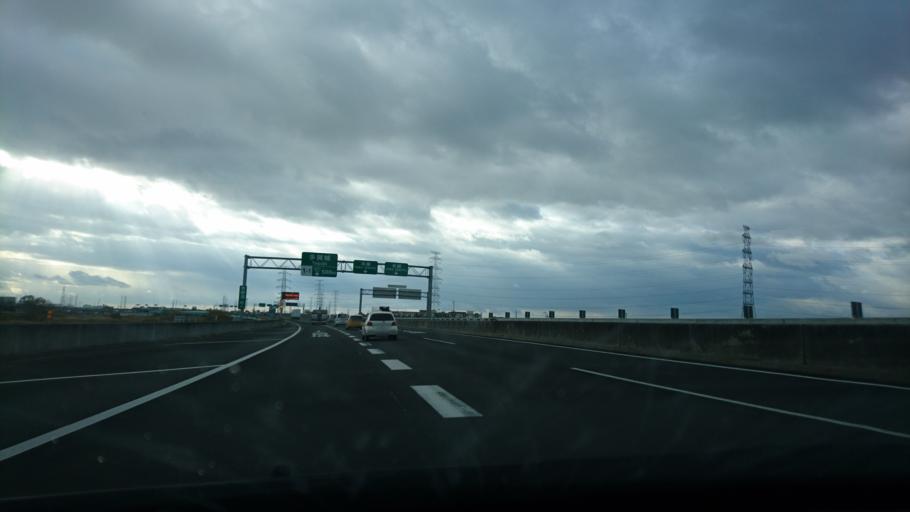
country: JP
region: Miyagi
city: Rifu
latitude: 38.3076
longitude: 140.9779
